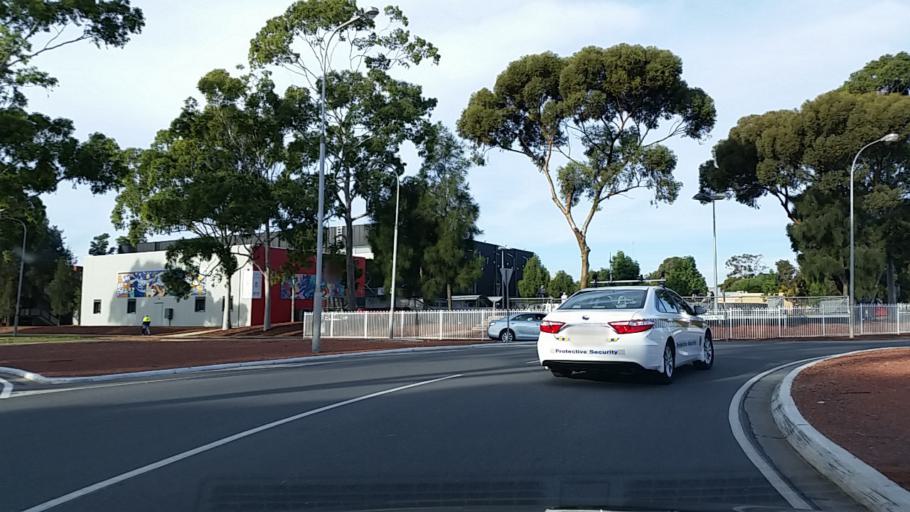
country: AU
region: South Australia
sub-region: Salisbury
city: Elizabeth
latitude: -34.7143
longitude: 138.6696
